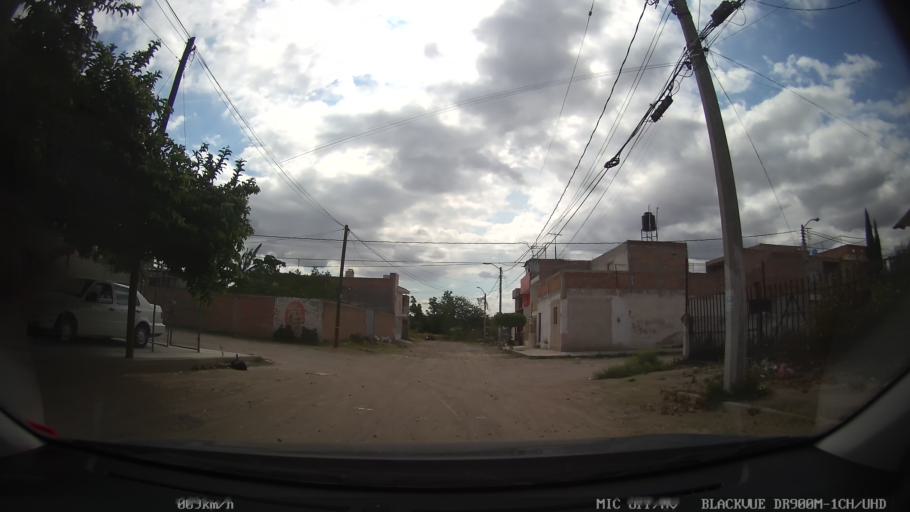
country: MX
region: Jalisco
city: Tonala
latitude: 20.6711
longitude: -103.2502
